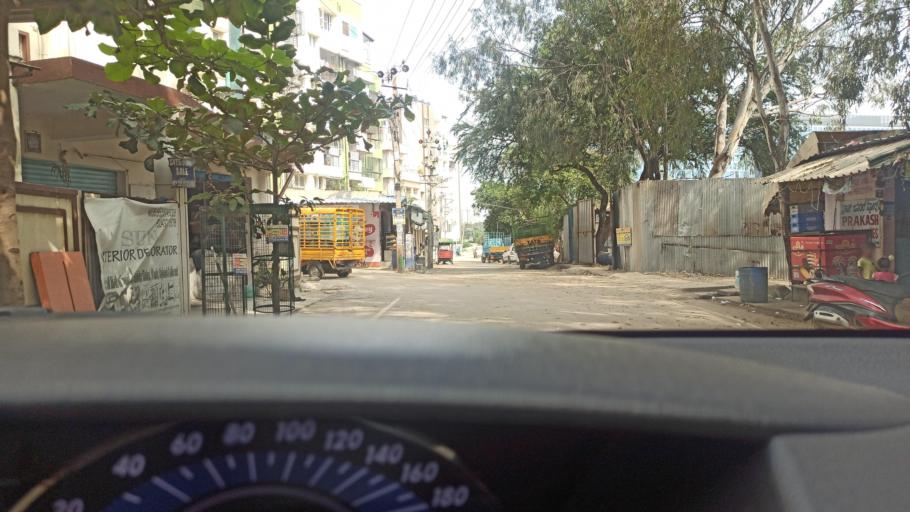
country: IN
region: Karnataka
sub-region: Bangalore Urban
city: Bangalore
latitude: 12.9856
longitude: 77.6883
